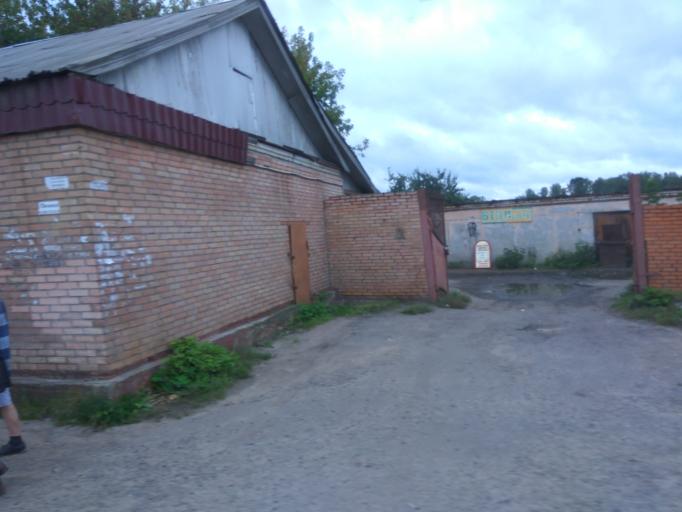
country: RU
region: Moskovskaya
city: Malyshevo
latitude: 55.4983
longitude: 38.3606
